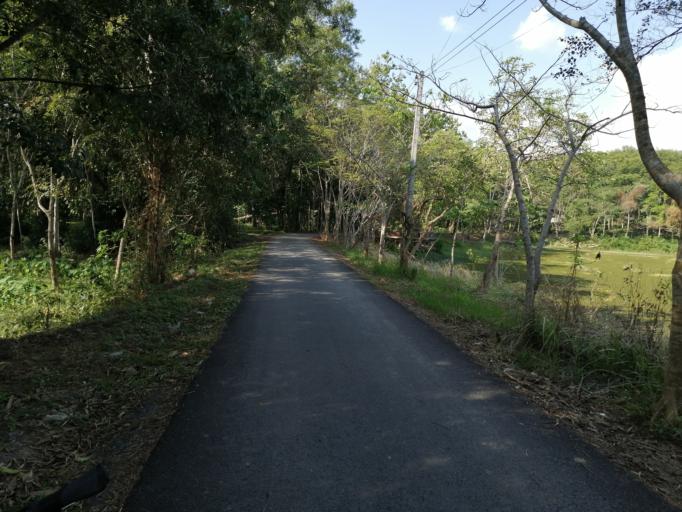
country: TH
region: Nakhon Si Thammarat
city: Thung Song
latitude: 8.2132
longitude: 99.6940
